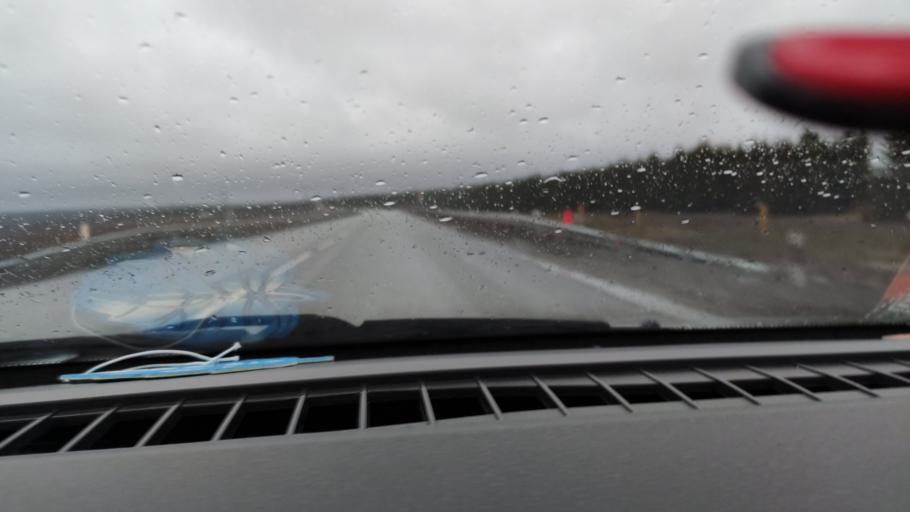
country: RU
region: Udmurtiya
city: Alnashi
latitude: 56.0829
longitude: 52.4089
